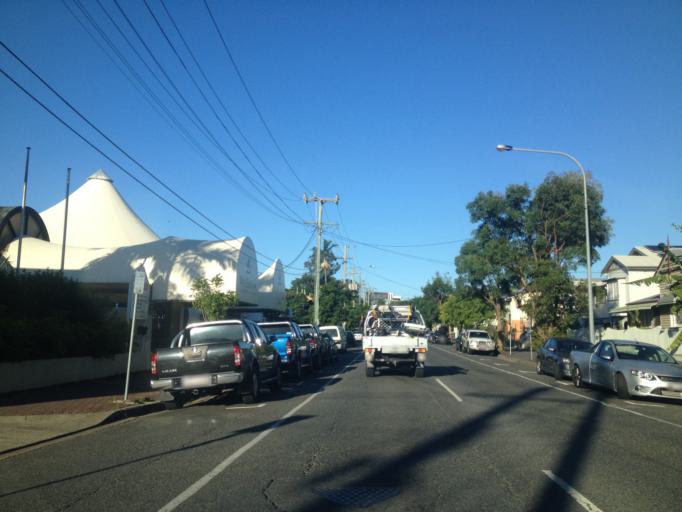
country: AU
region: Queensland
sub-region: Brisbane
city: Milton
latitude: -27.4802
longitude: 153.0055
